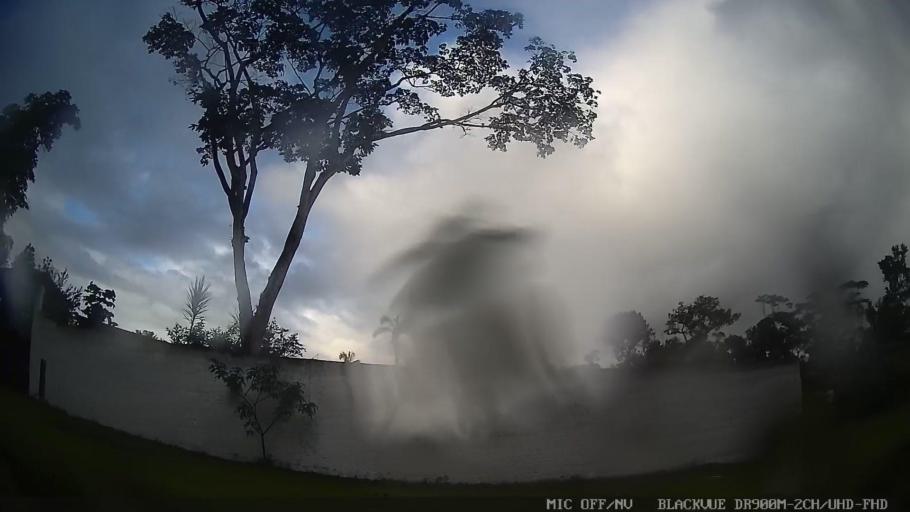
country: BR
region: Sao Paulo
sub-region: Peruibe
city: Peruibe
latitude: -24.2258
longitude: -46.9144
